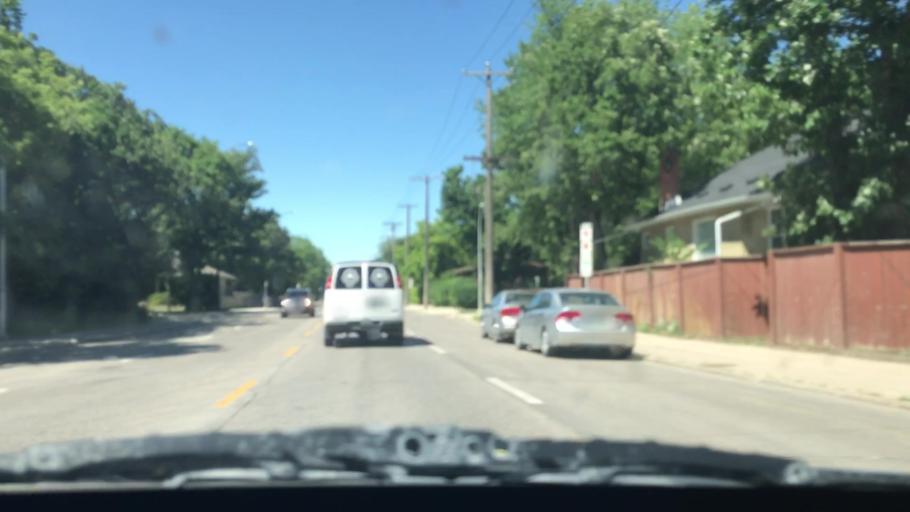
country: CA
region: Manitoba
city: Winnipeg
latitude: 49.8709
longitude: -97.1636
